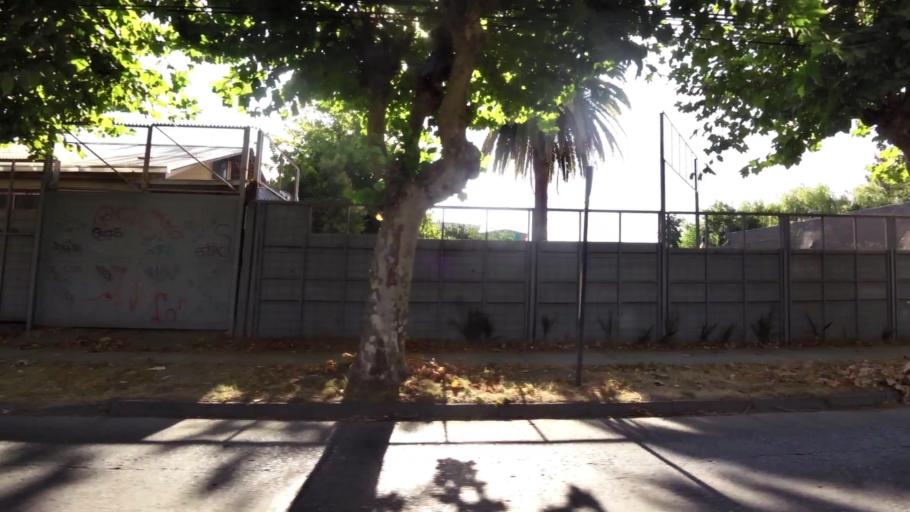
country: CL
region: Maule
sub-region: Provincia de Talca
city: Talca
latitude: -35.4383
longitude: -71.6664
